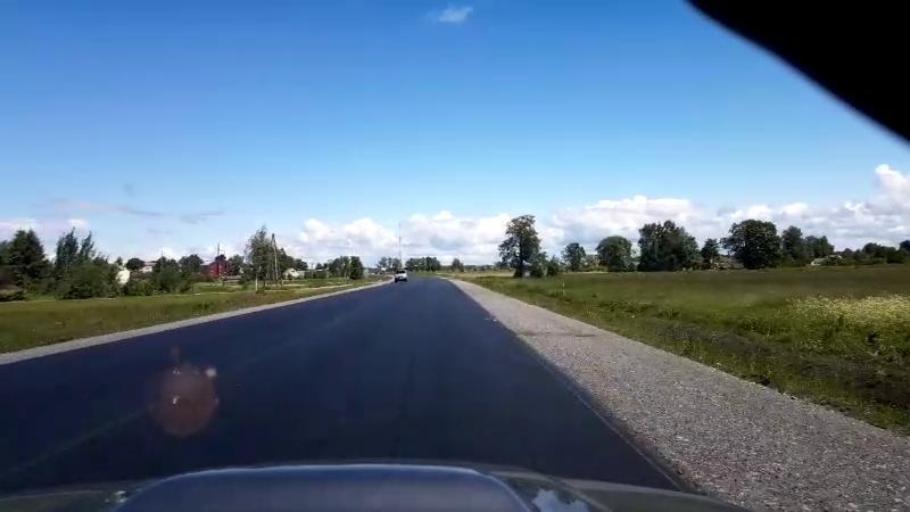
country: LV
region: Salacgrivas
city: Ainazi
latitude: 57.8556
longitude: 24.3638
